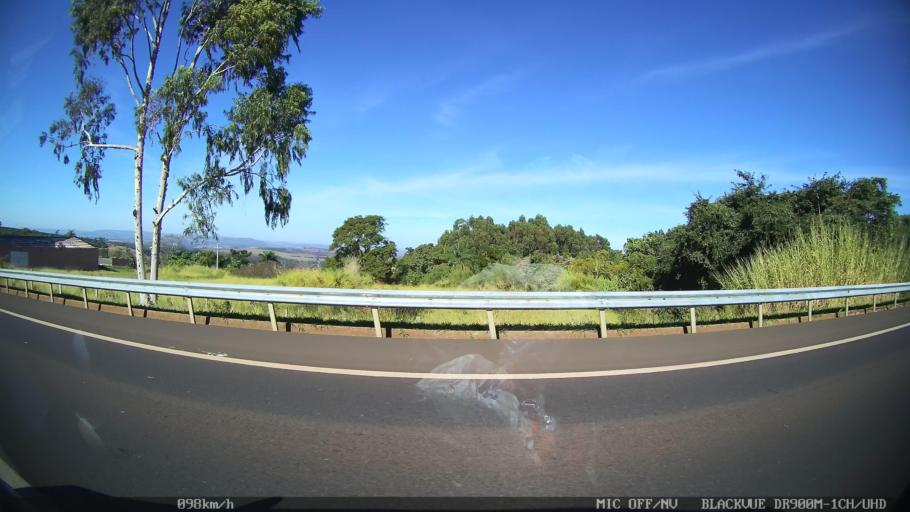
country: BR
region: Sao Paulo
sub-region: Franca
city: Franca
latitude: -20.5782
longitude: -47.3446
